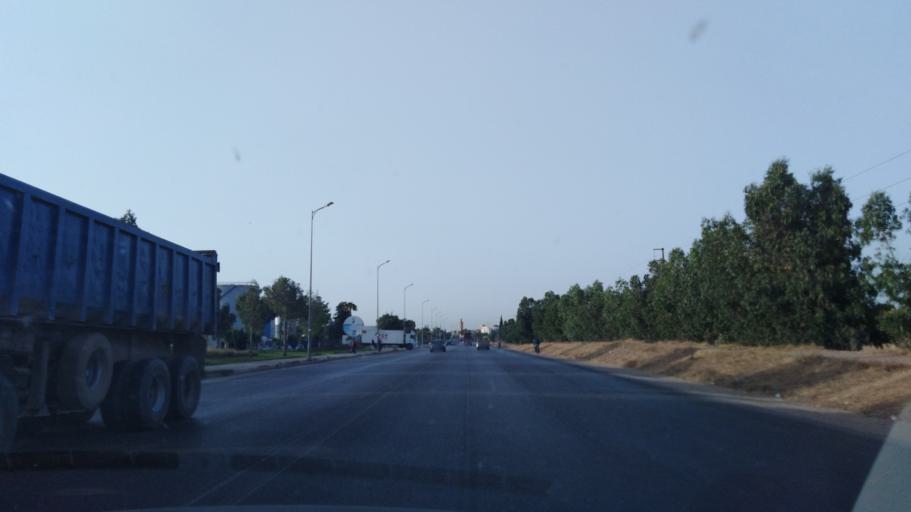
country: MA
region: Chaouia-Ouardigha
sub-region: Settat Province
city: Berrechid
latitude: 33.2528
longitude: -7.5838
